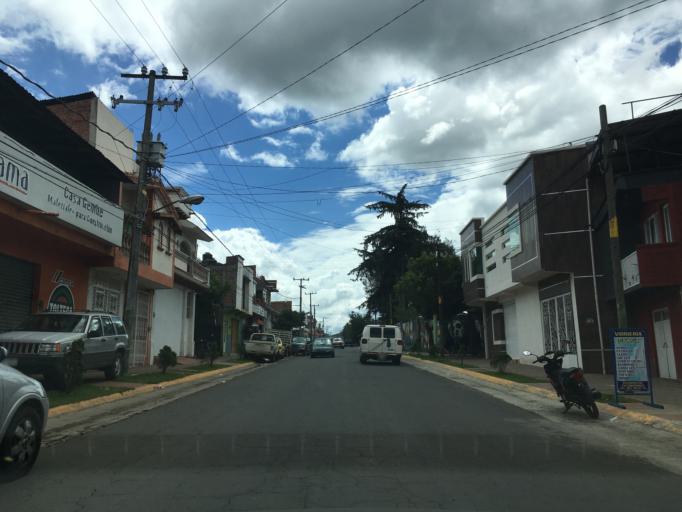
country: MX
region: Michoacan
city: Cheran
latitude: 19.6813
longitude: -101.9547
